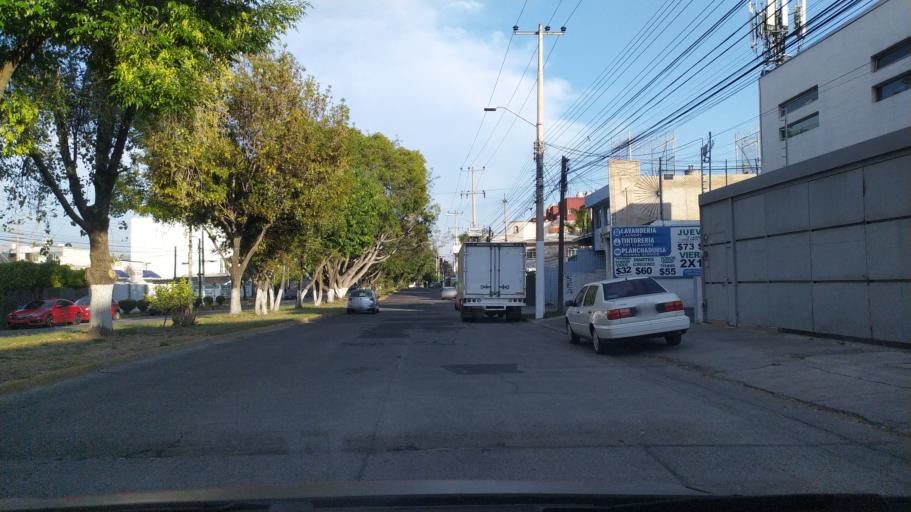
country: MX
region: Jalisco
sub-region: Tlajomulco de Zuniga
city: La Tijera
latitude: 20.6265
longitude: -103.4234
